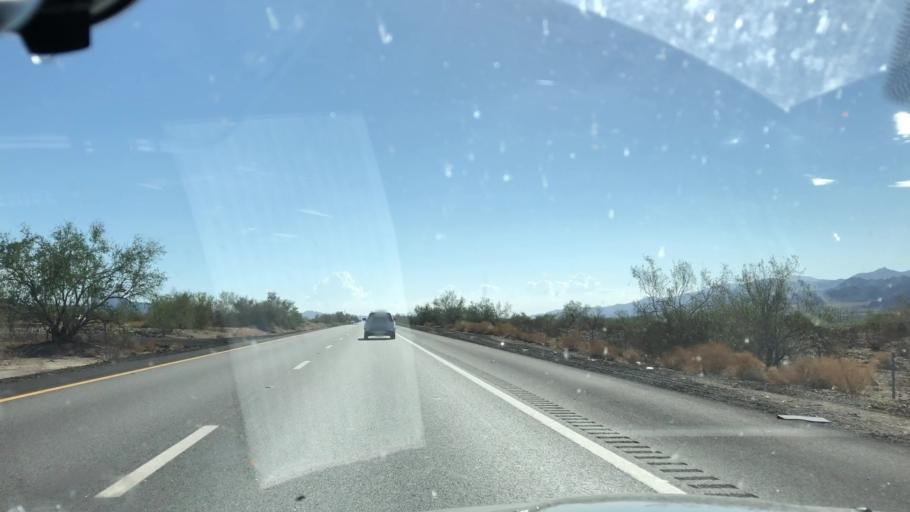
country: US
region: California
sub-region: Imperial County
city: Niland
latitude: 33.6974
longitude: -115.4766
